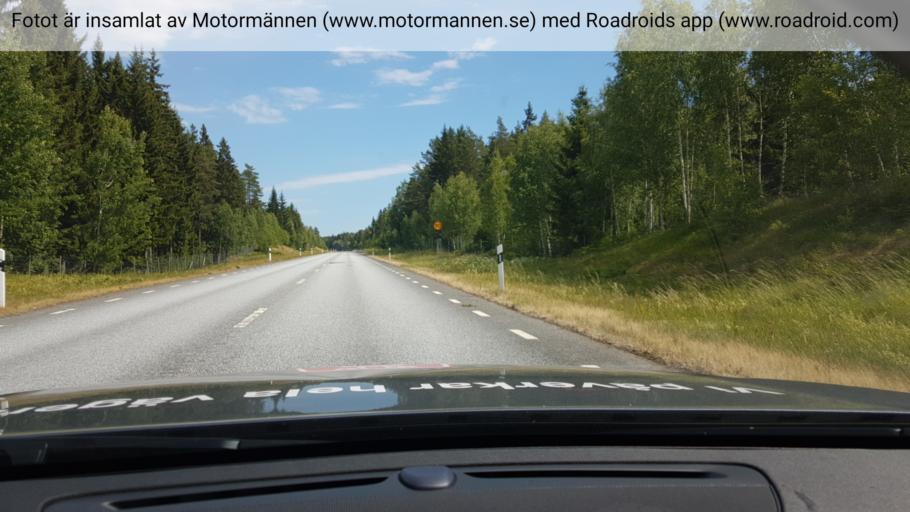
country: SE
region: Uppsala
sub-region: Osthammars Kommun
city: Gimo
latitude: 60.1657
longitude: 18.2195
